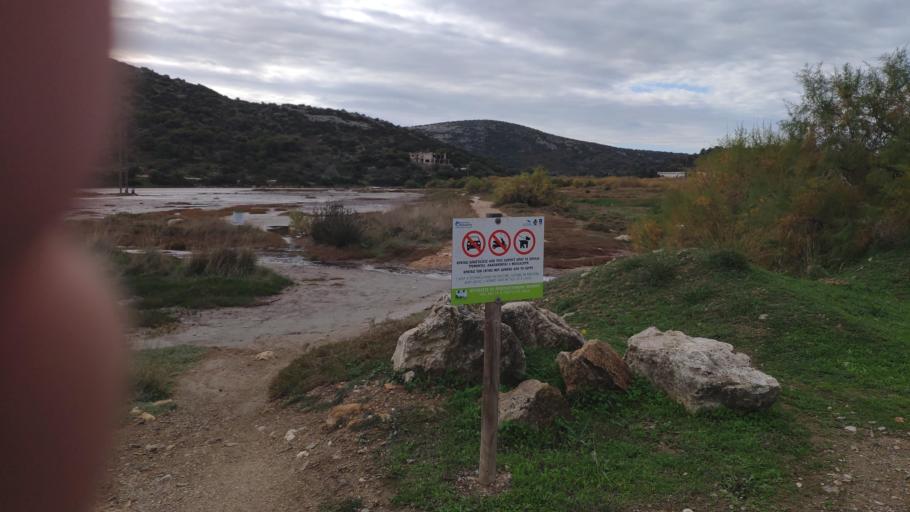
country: GR
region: Attica
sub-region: Nomarchia Anatolikis Attikis
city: Limin Mesoyaias
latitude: 37.9277
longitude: 24.0031
